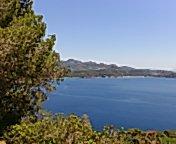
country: IT
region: Tuscany
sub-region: Provincia di Livorno
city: Capoliveri
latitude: 42.7482
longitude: 10.3192
